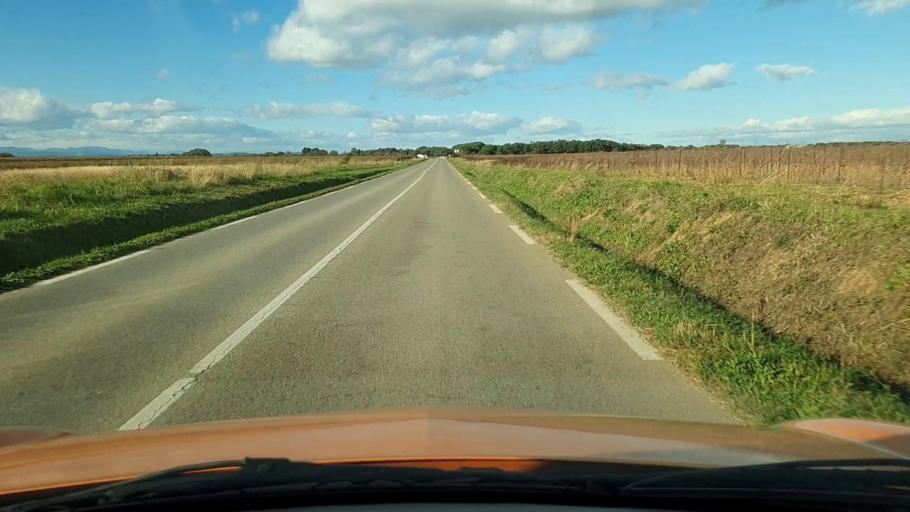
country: FR
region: Languedoc-Roussillon
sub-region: Departement du Gard
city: Vauvert
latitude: 43.6761
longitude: 4.2798
